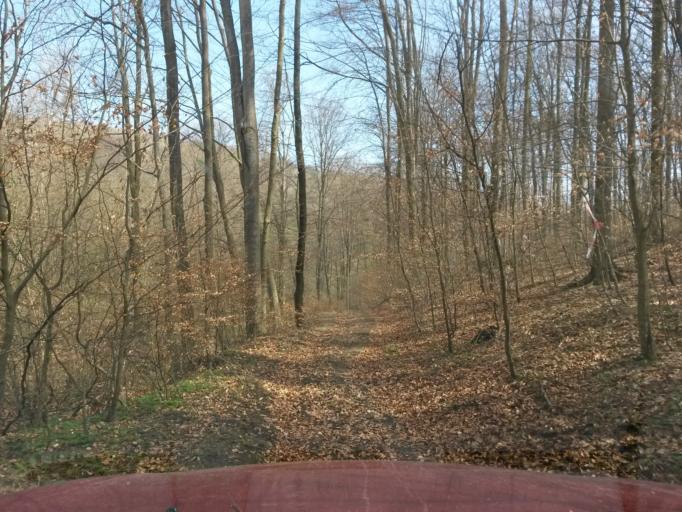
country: SK
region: Presovsky
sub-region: Okres Presov
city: Presov
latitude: 48.9371
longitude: 21.1429
